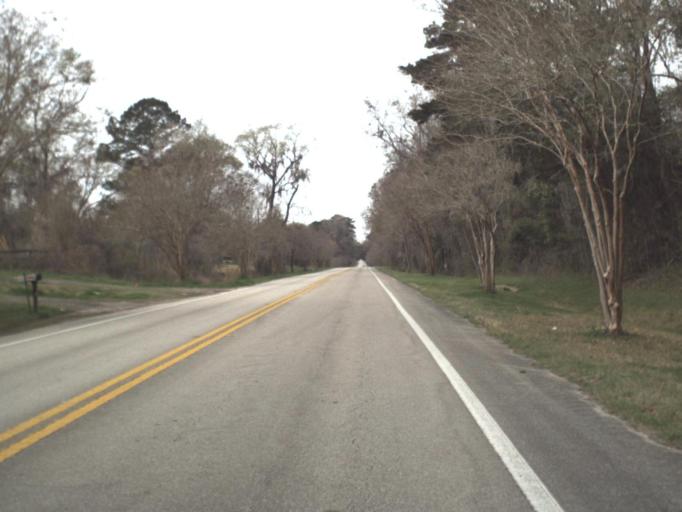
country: US
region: Florida
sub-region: Jefferson County
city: Monticello
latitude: 30.5350
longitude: -83.9423
